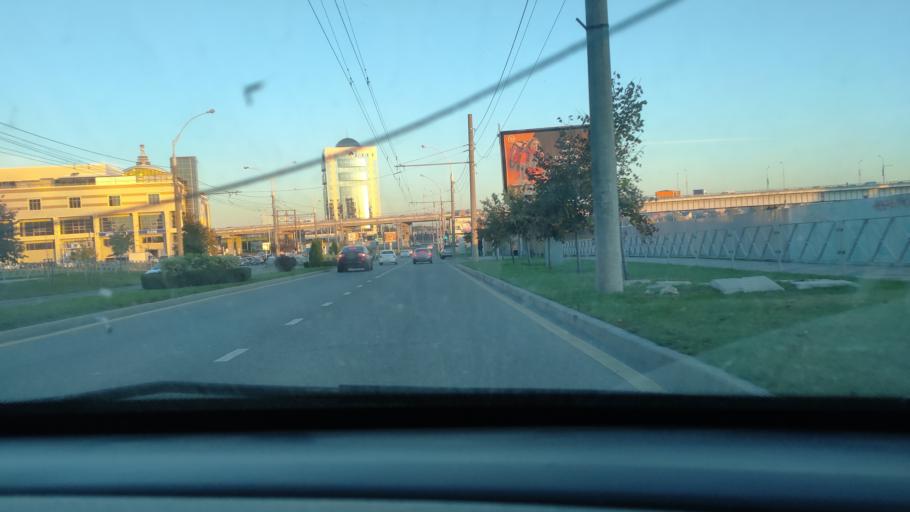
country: RU
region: Krasnodarskiy
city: Krasnodar
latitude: 45.0375
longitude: 38.9509
